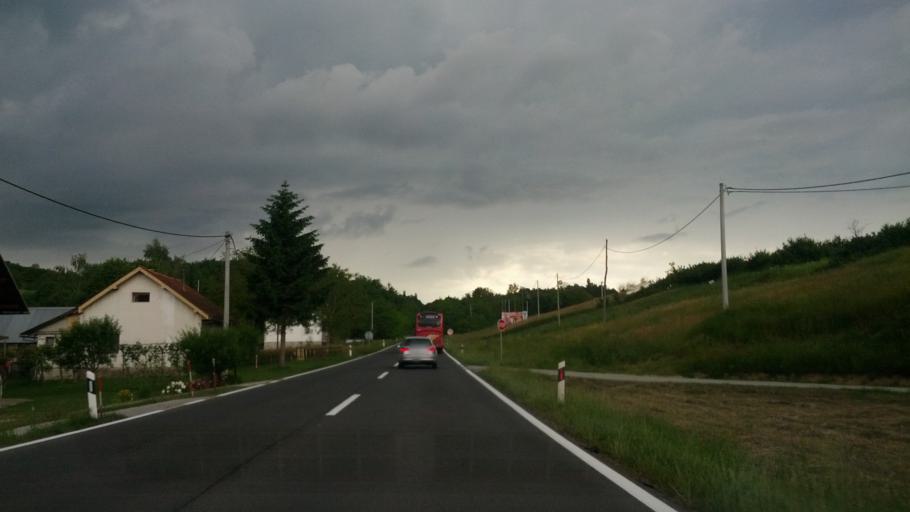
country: HR
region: Karlovacka
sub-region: Grad Karlovac
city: Karlovac
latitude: 45.4329
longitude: 15.5978
